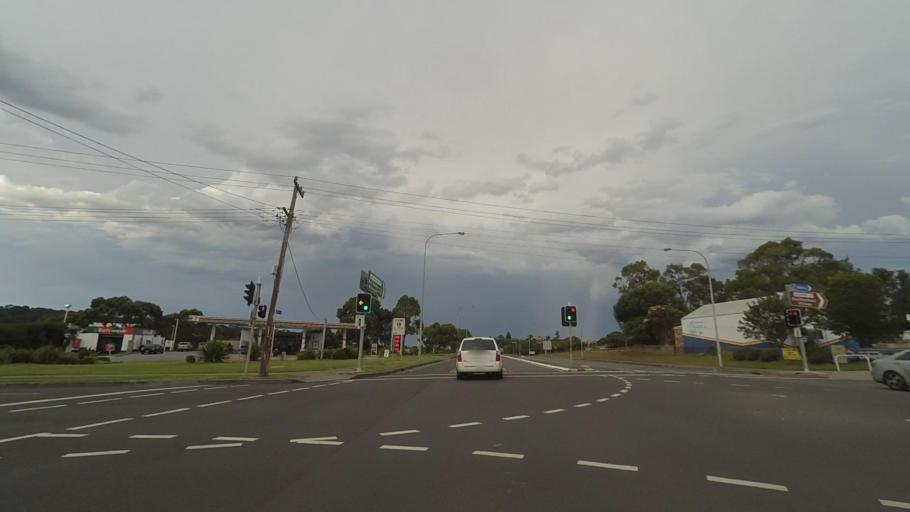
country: AU
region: New South Wales
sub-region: Shellharbour
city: Shellharbour Village
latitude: -34.5810
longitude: 150.8610
